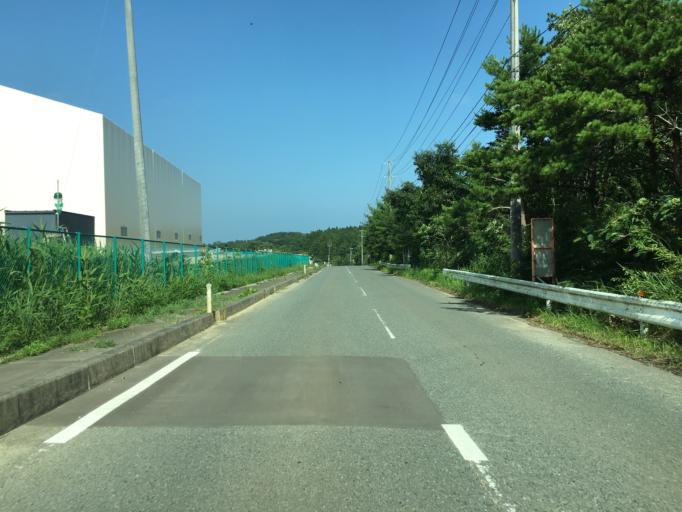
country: JP
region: Miyagi
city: Marumori
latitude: 37.9021
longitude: 140.8972
